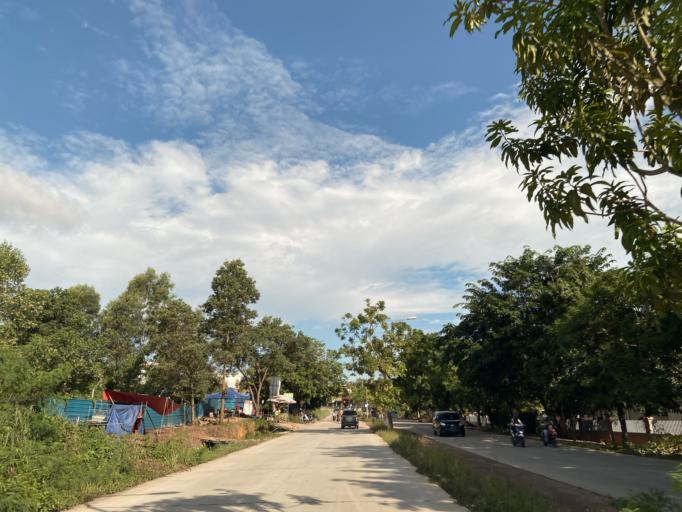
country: SG
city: Singapore
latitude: 1.1102
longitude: 104.0782
